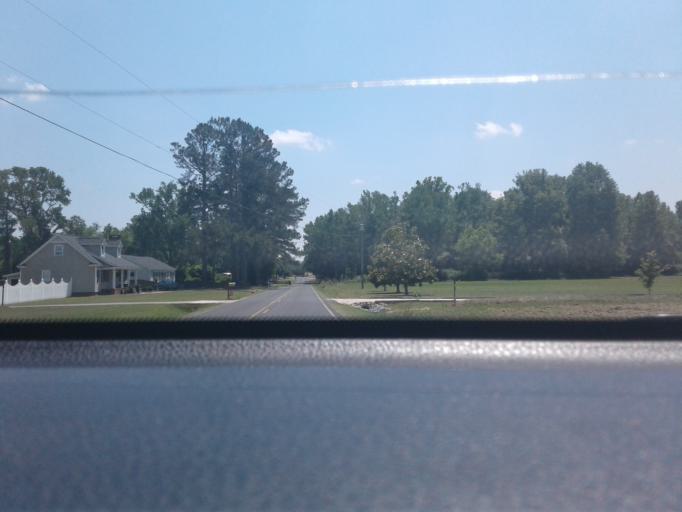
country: US
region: North Carolina
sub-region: Harnett County
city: Dunn
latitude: 35.3430
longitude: -78.5782
